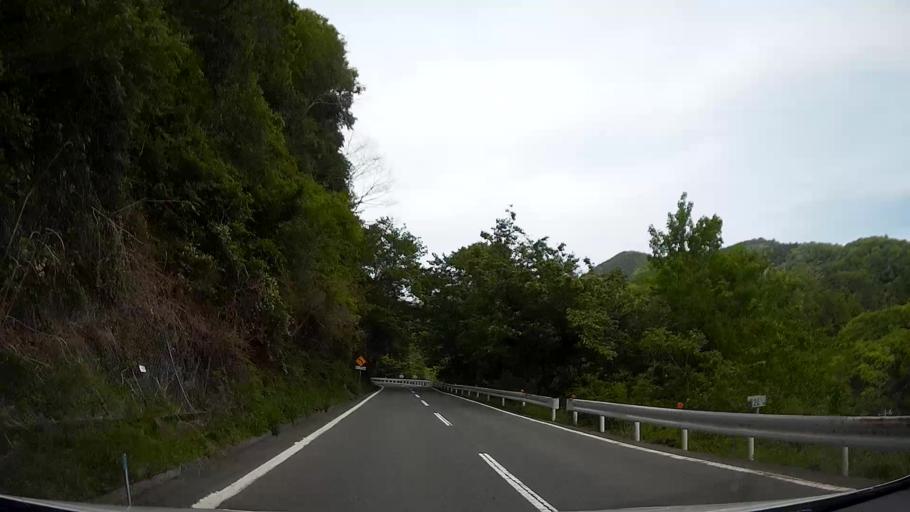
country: JP
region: Shizuoka
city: Ito
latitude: 34.9680
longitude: 139.0422
